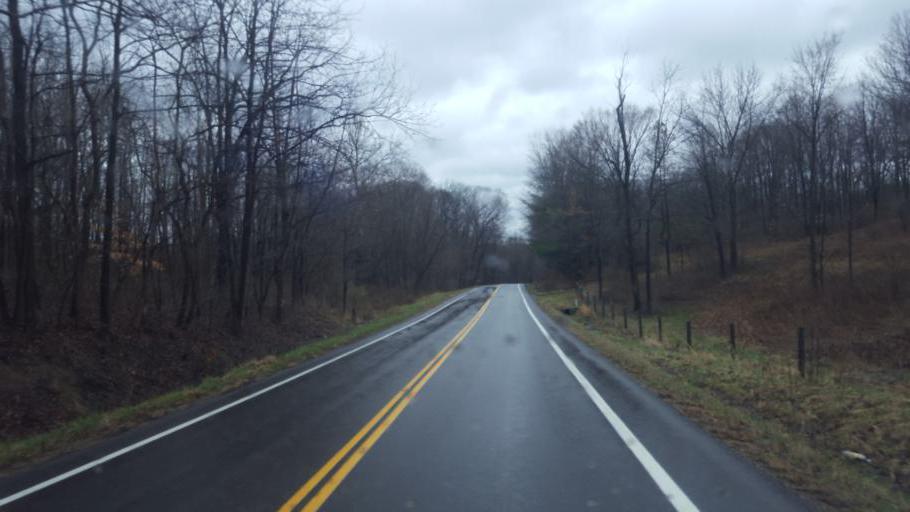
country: US
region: Ohio
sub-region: Sandusky County
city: Bellville
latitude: 40.6227
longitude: -82.3975
